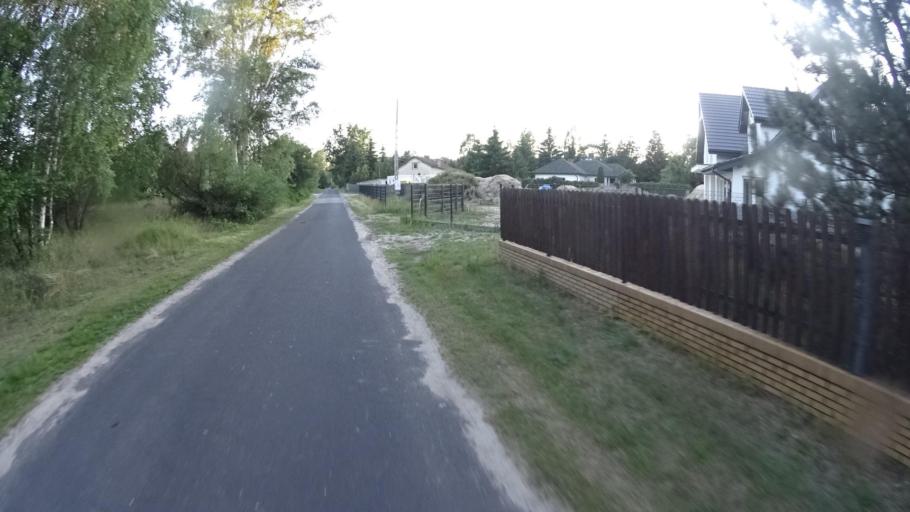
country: PL
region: Masovian Voivodeship
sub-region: Powiat warszawski zachodni
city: Jozefow
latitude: 52.2751
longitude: 20.7015
